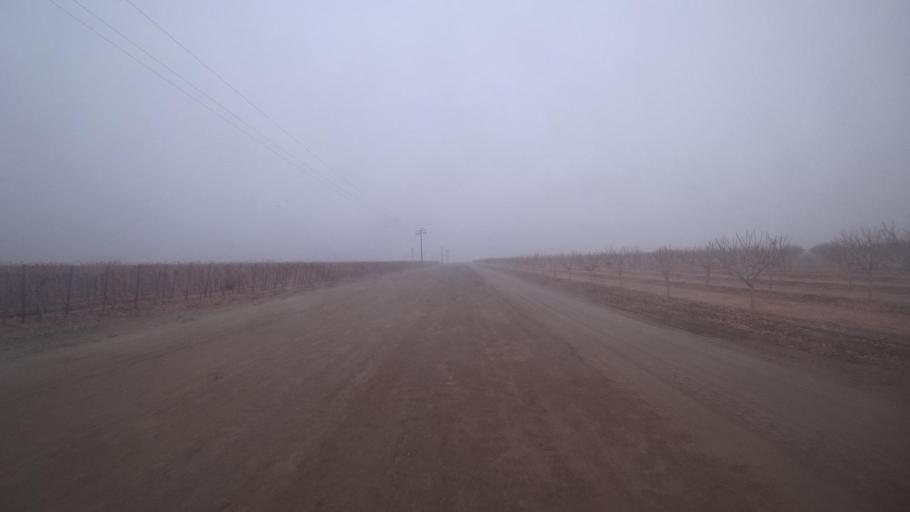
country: US
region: California
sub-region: Kern County
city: Buttonwillow
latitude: 35.4641
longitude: -119.5649
